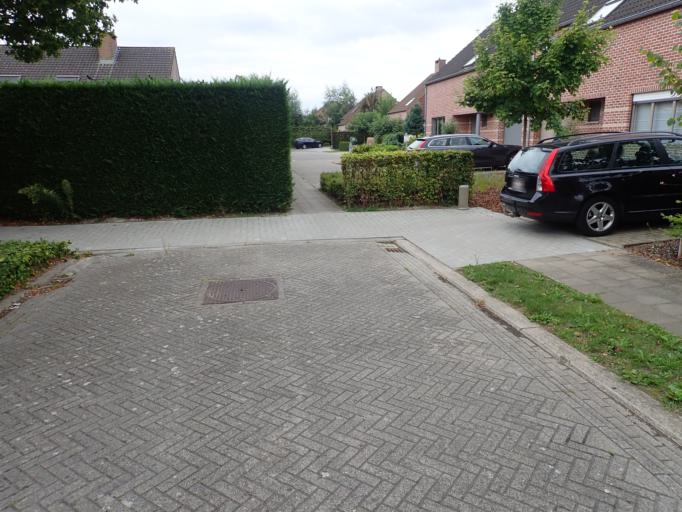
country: BE
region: Flanders
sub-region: Provincie Antwerpen
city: Niel
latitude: 51.0909
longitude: 4.3236
